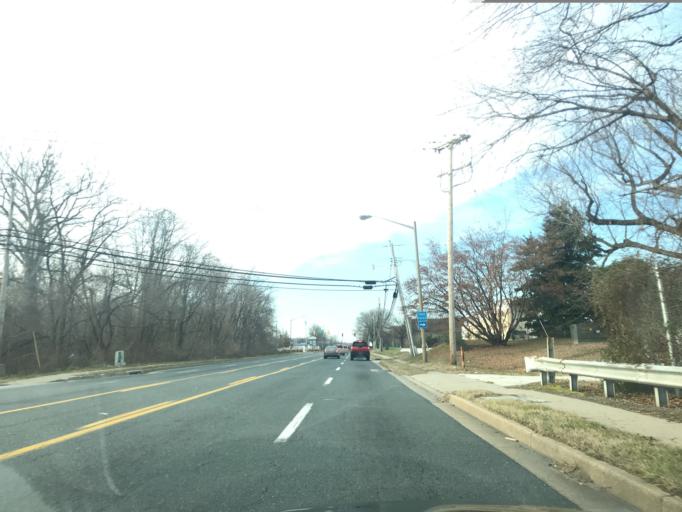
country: US
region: Maryland
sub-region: Baltimore County
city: Rossville
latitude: 39.3327
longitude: -76.4751
